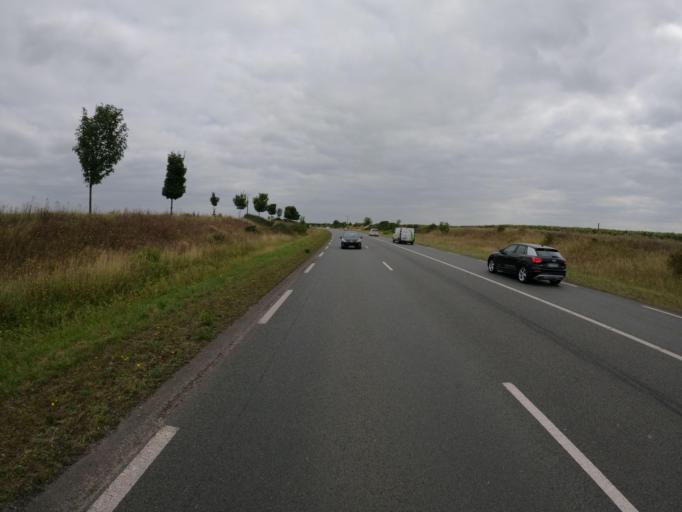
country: FR
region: Poitou-Charentes
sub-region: Departement des Deux-Sevres
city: Vouille
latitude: 46.3006
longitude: -0.3463
